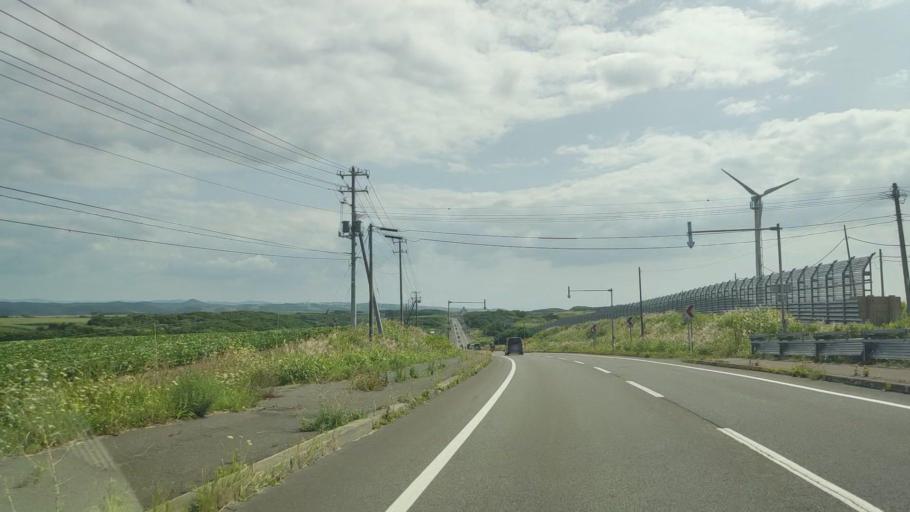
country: JP
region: Hokkaido
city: Rumoi
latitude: 44.3007
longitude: 141.6529
